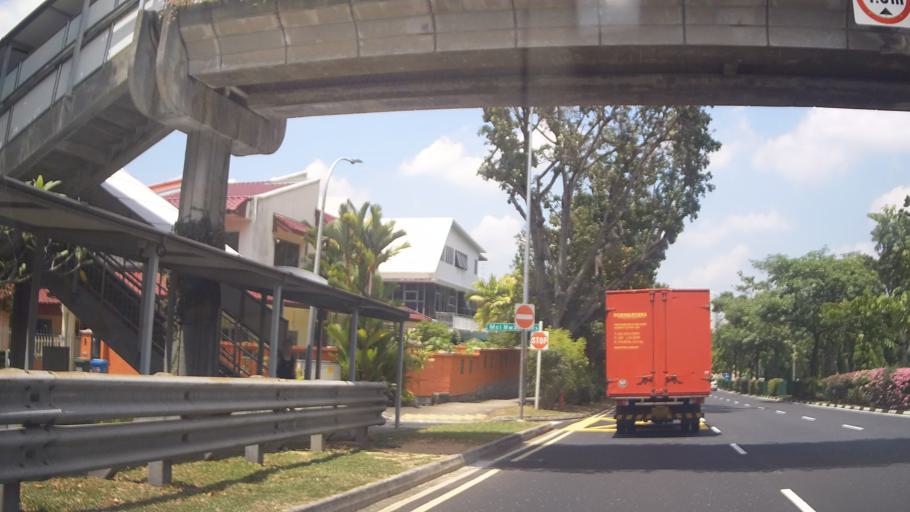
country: SG
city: Singapore
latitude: 1.3545
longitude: 103.8608
